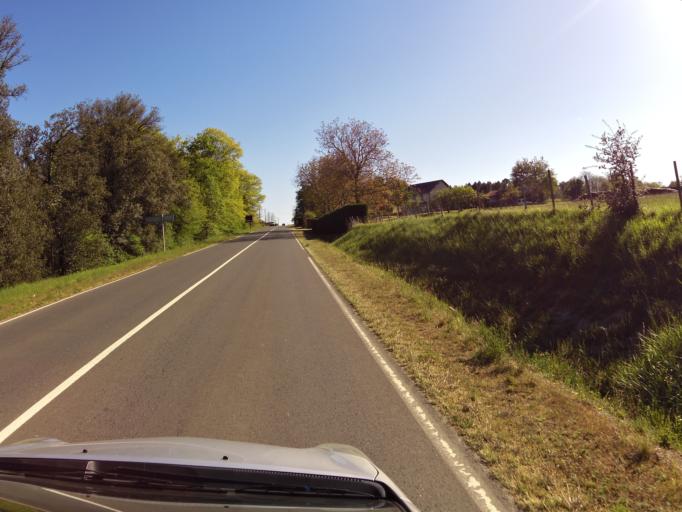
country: FR
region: Aquitaine
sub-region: Departement de la Dordogne
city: Montignac
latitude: 44.9943
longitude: 1.2418
